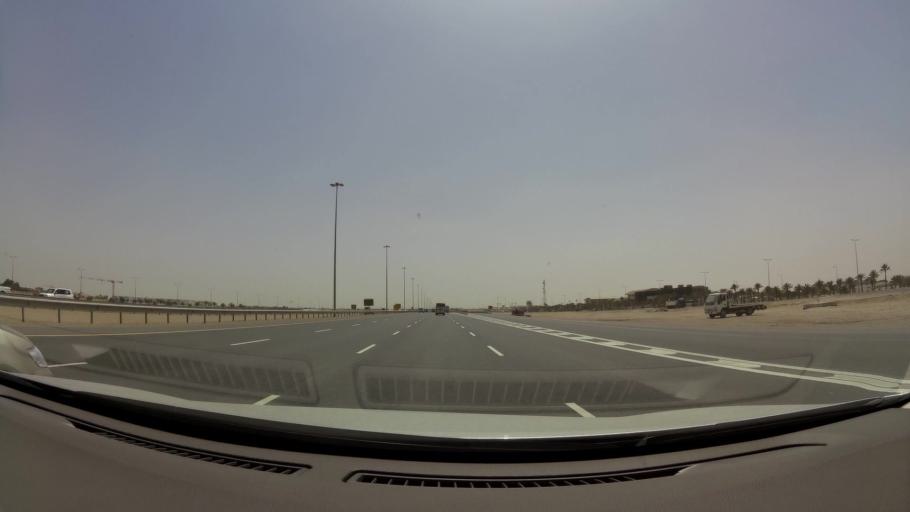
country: QA
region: Baladiyat Umm Salal
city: Umm Salal `Ali
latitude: 25.4609
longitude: 51.4086
